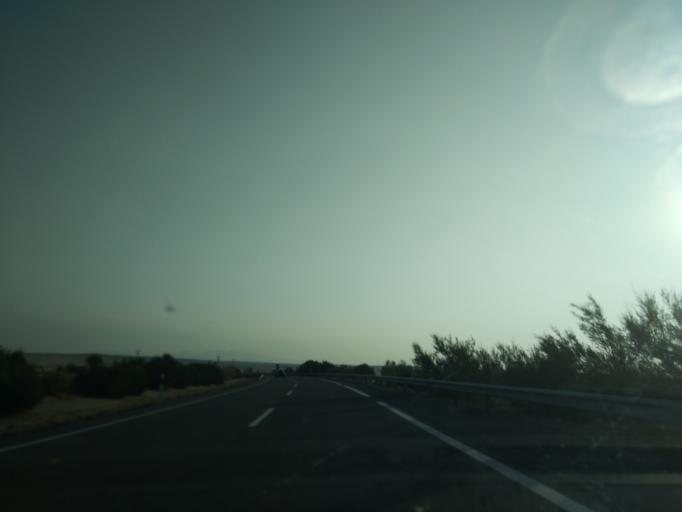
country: ES
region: Castille and Leon
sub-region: Provincia de Avila
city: Mediana de Voltoya
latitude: 40.6986
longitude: -4.5785
